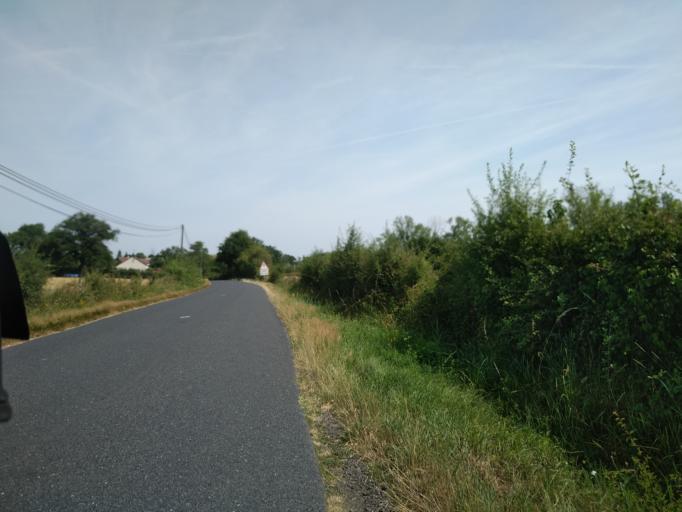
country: FR
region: Auvergne
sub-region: Departement de l'Allier
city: Molinet
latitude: 46.4196
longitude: 3.9768
